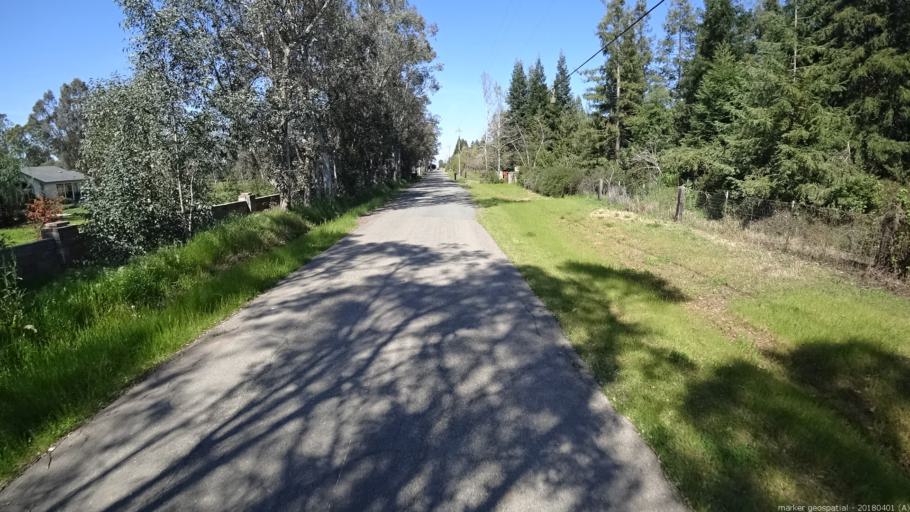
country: US
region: California
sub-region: Sacramento County
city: Wilton
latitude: 38.3834
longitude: -121.2194
